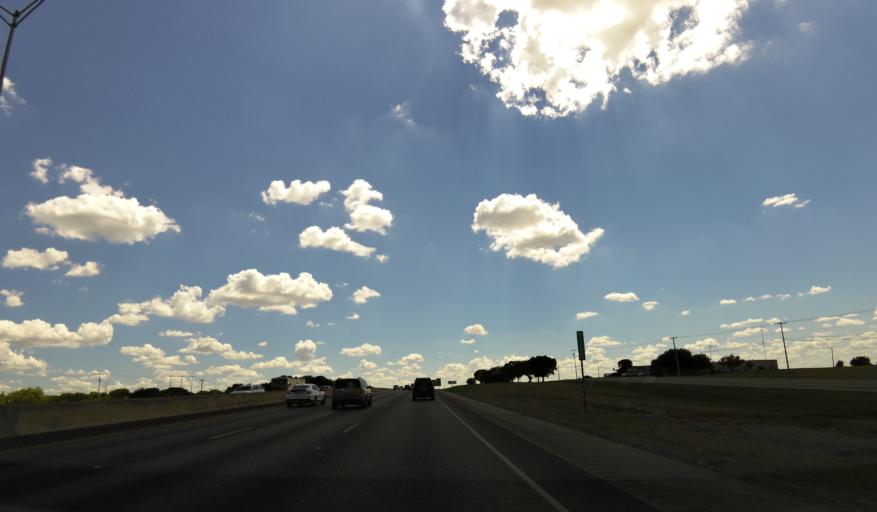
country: US
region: Texas
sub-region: Guadalupe County
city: Northcliff
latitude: 29.6347
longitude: -98.2221
